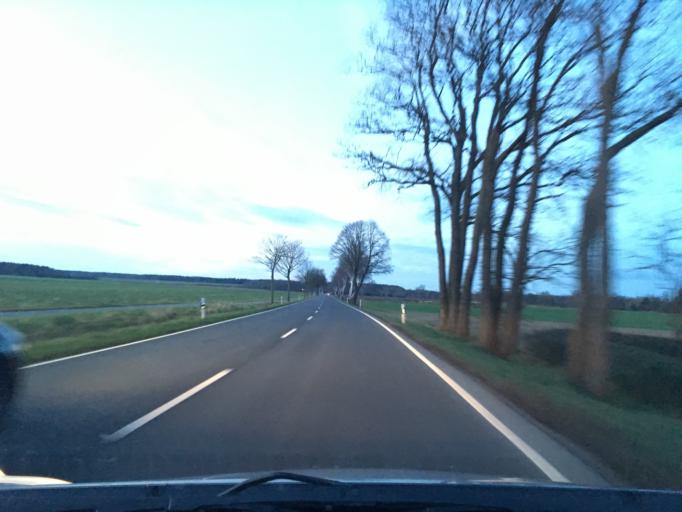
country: DE
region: Lower Saxony
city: Luechow
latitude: 52.9850
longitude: 11.1254
